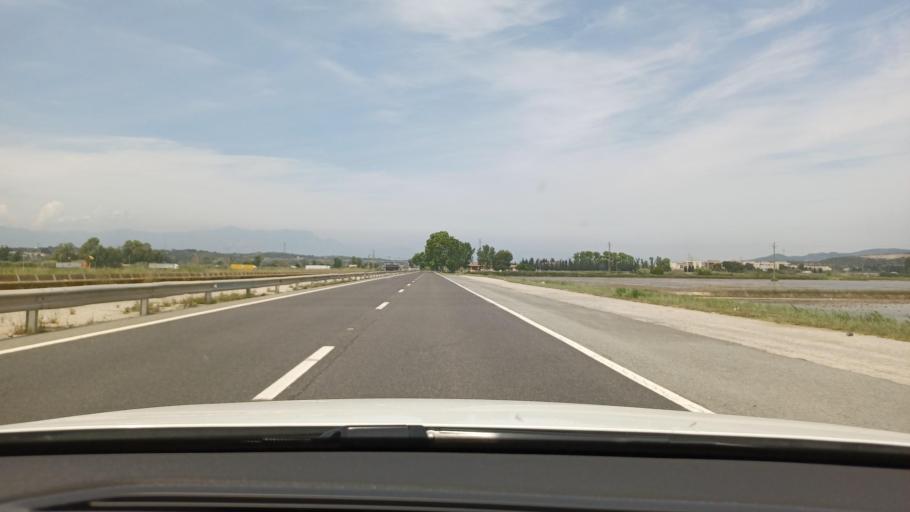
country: ES
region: Catalonia
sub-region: Provincia de Tarragona
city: Amposta
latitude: 40.7154
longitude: 0.5913
